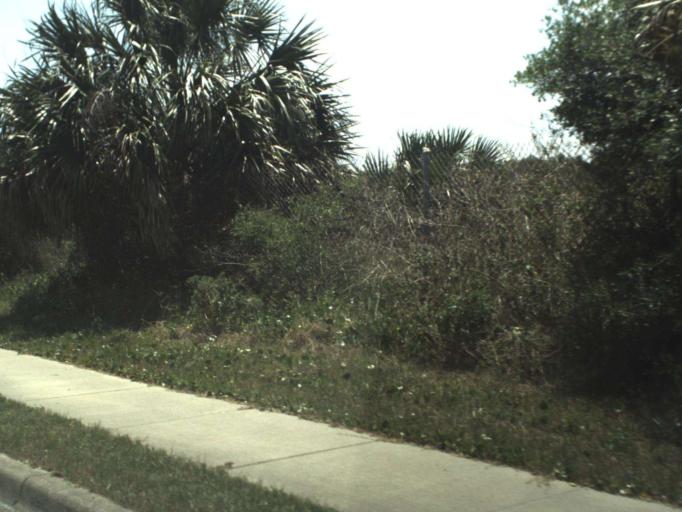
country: US
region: Florida
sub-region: Volusia County
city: New Smyrna Beach
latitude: 29.0204
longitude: -80.9251
